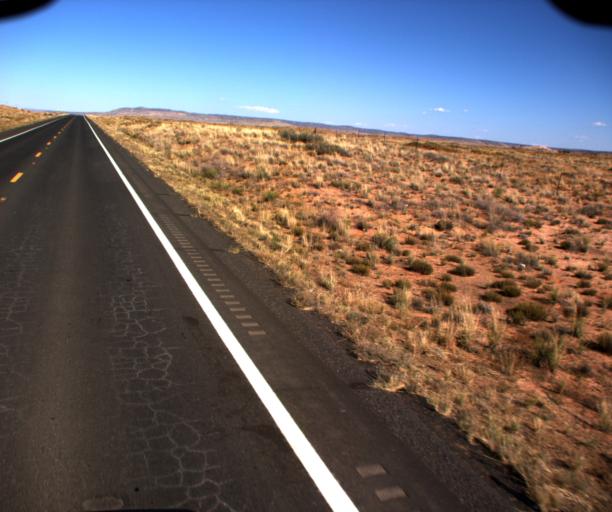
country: US
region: Arizona
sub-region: Coconino County
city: Tuba City
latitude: 36.2926
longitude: -110.9887
